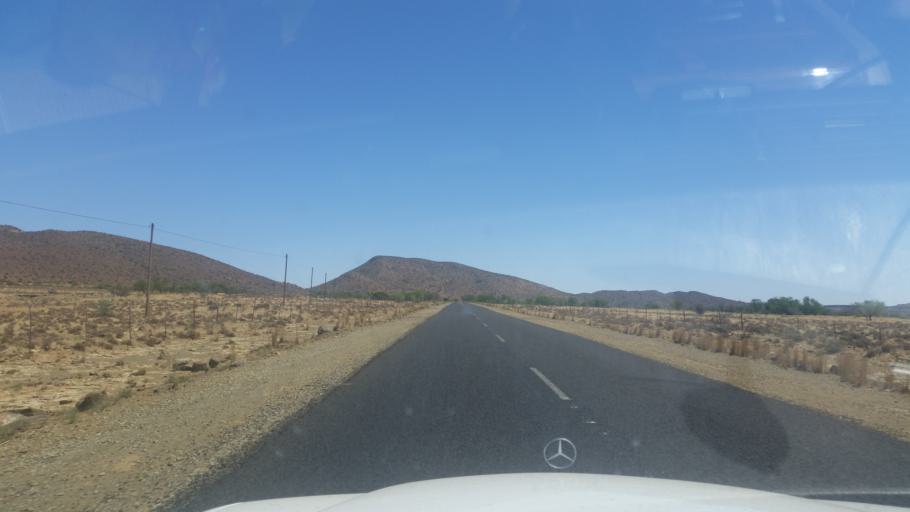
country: ZA
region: Northern Cape
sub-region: Pixley ka Seme District Municipality
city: Colesberg
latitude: -30.6293
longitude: 25.4373
